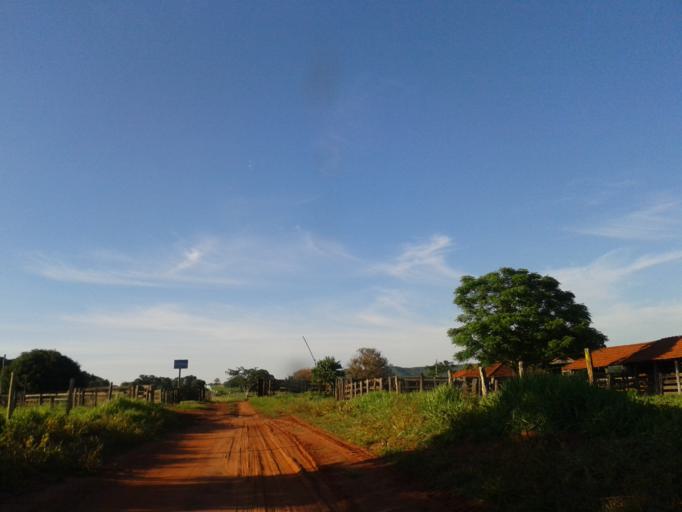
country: BR
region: Minas Gerais
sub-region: Santa Vitoria
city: Santa Vitoria
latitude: -18.9589
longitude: -49.8651
